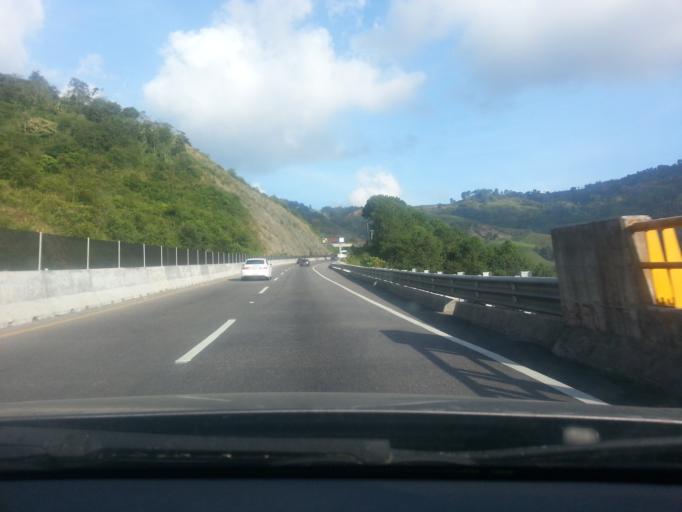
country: MX
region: Puebla
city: Necaxa
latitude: 20.2399
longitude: -98.0347
